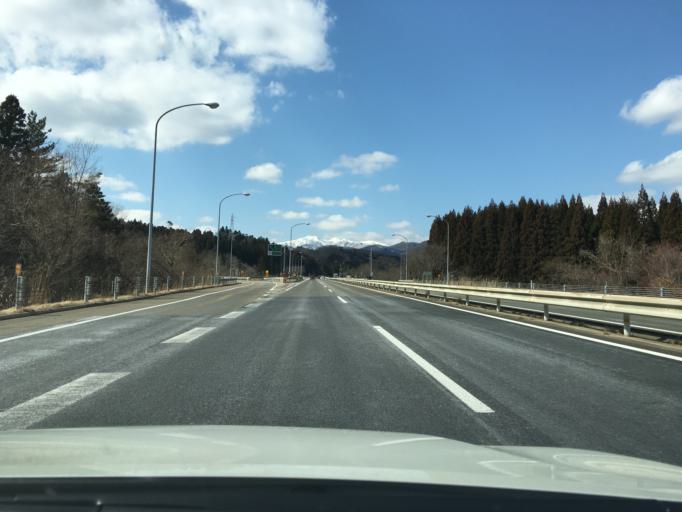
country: JP
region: Miyagi
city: Okawara
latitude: 38.1741
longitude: 140.6246
